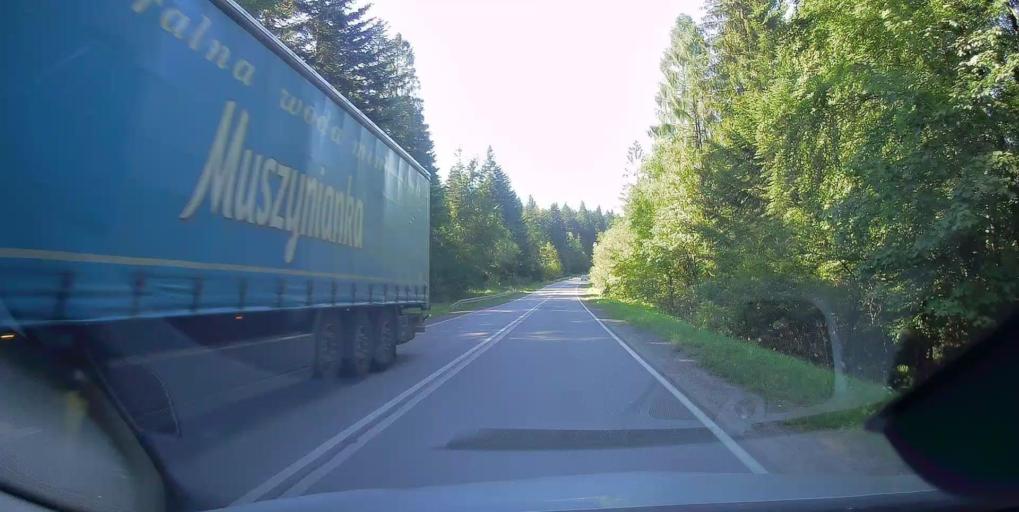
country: PL
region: Lesser Poland Voivodeship
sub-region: Powiat nowosadecki
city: Krynica-Zdroj
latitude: 49.4525
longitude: 20.9532
